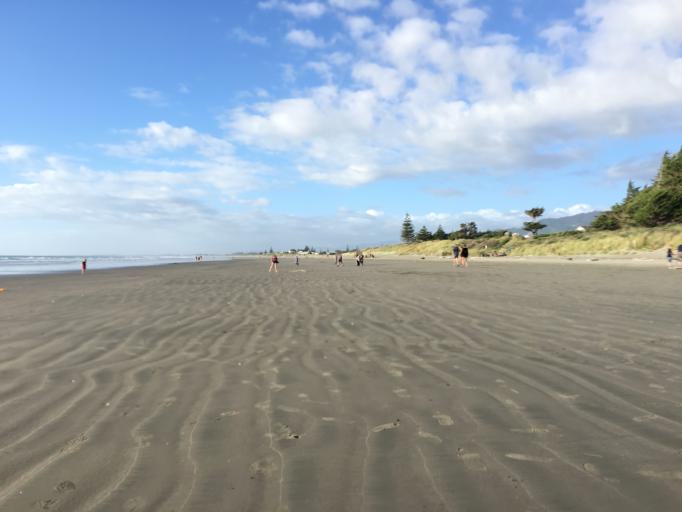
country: NZ
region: Wellington
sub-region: Kapiti Coast District
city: Paraparaumu
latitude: -40.8609
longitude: 175.0224
